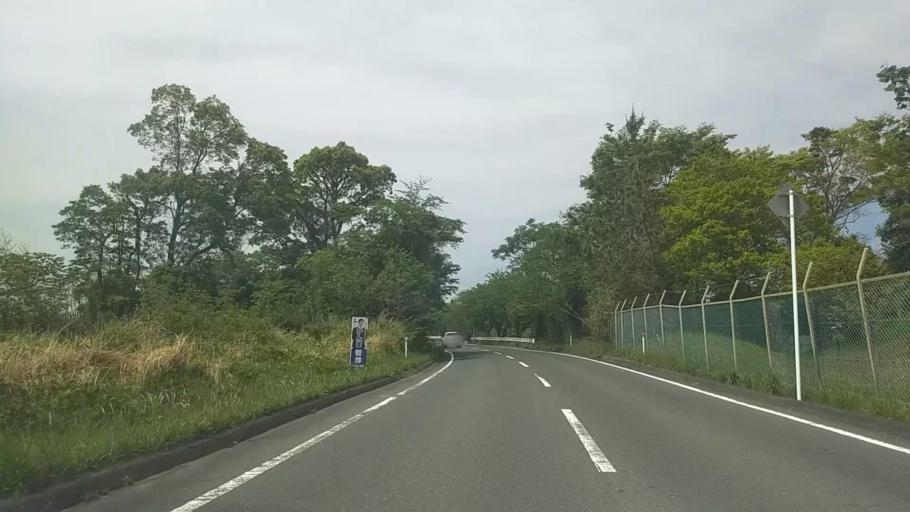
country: JP
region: Shizuoka
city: Kosai-shi
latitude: 34.7829
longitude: 137.5745
